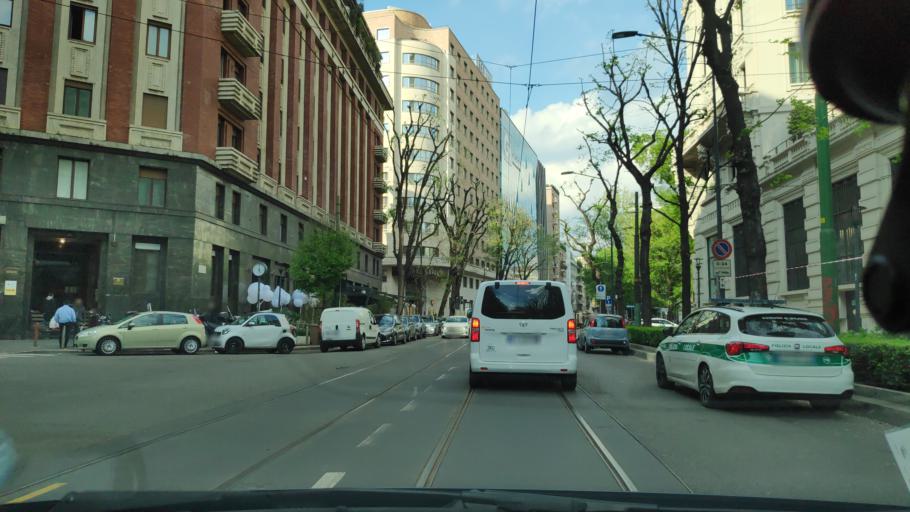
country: IT
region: Lombardy
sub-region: Citta metropolitana di Milano
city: Milano
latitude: 45.4860
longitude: 9.2014
